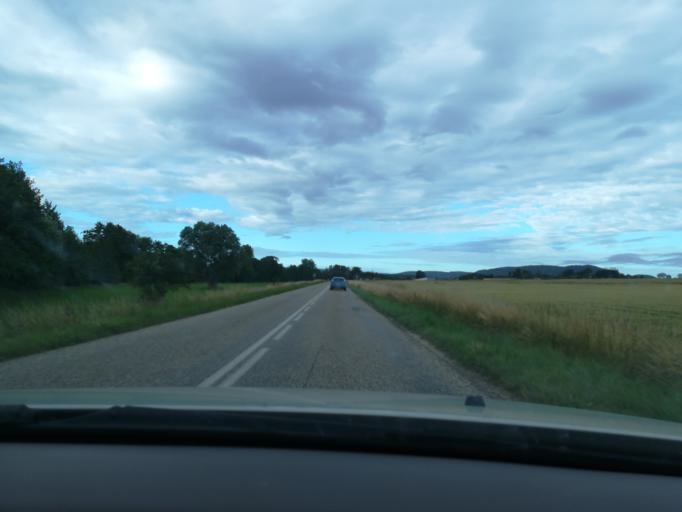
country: FR
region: Alsace
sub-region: Departement du Bas-Rhin
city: Bouxwiller
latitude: 48.8200
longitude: 7.4457
